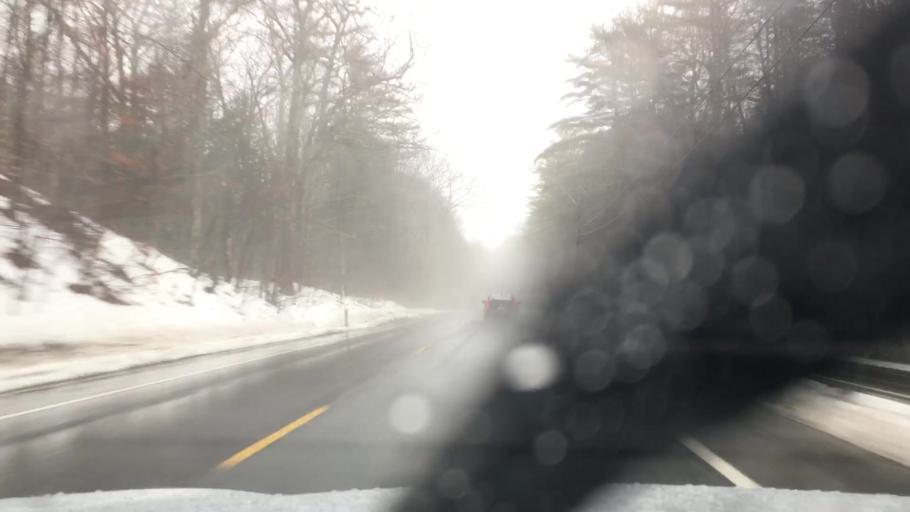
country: US
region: Massachusetts
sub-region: Franklin County
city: Orange
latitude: 42.5265
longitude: -72.3215
